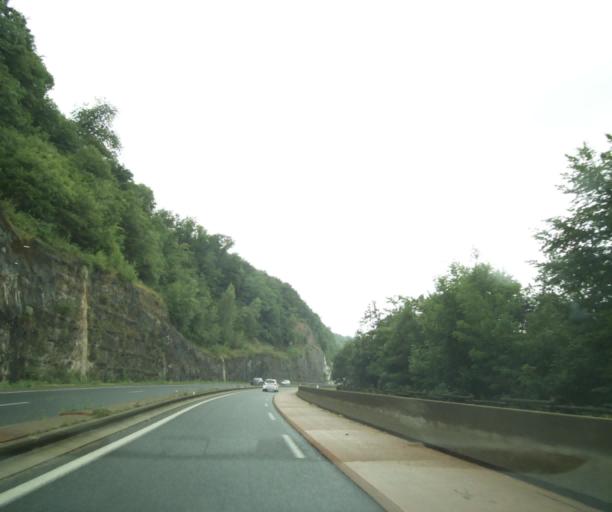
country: FR
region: Midi-Pyrenees
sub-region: Departement de l'Aveyron
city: Olemps
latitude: 44.3471
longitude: 2.5574
